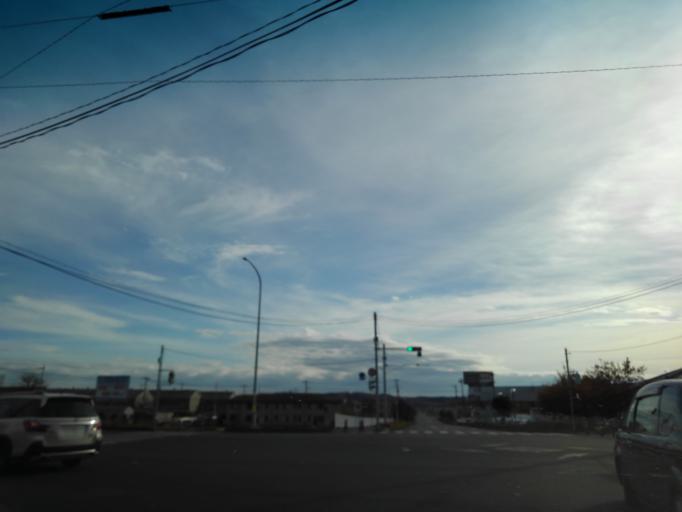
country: JP
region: Saitama
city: Hanno
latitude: 35.8589
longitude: 139.3367
